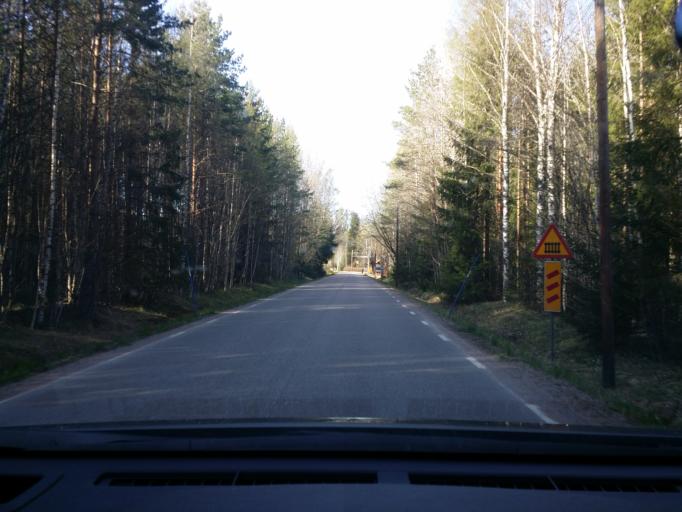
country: SE
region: Dalarna
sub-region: Avesta Kommun
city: Avesta
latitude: 60.0686
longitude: 16.3484
